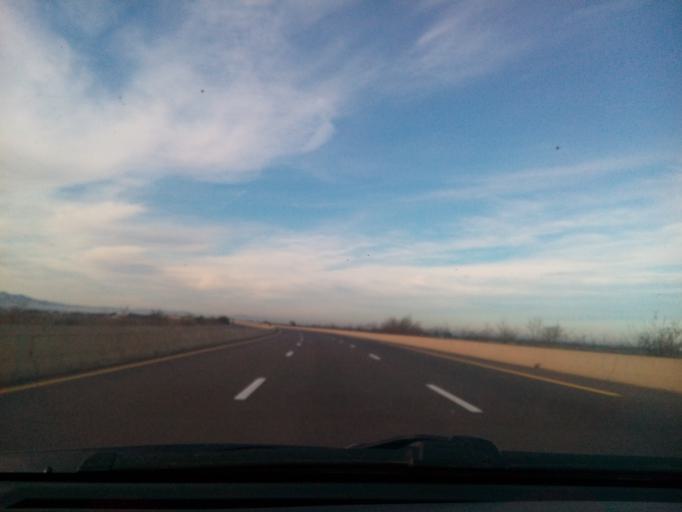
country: DZ
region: Mascara
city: Mascara
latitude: 35.6515
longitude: 0.1075
